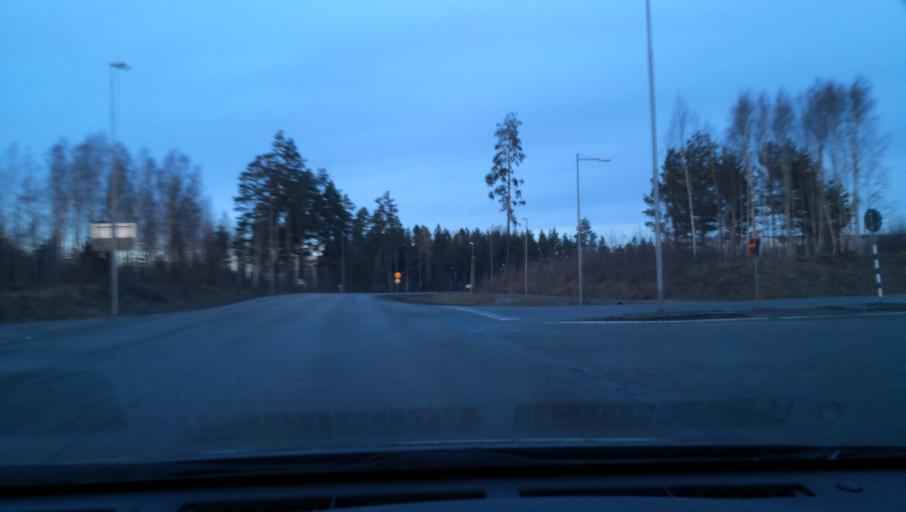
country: SE
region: OErebro
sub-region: Orebro Kommun
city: Orebro
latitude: 59.2406
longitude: 15.1201
